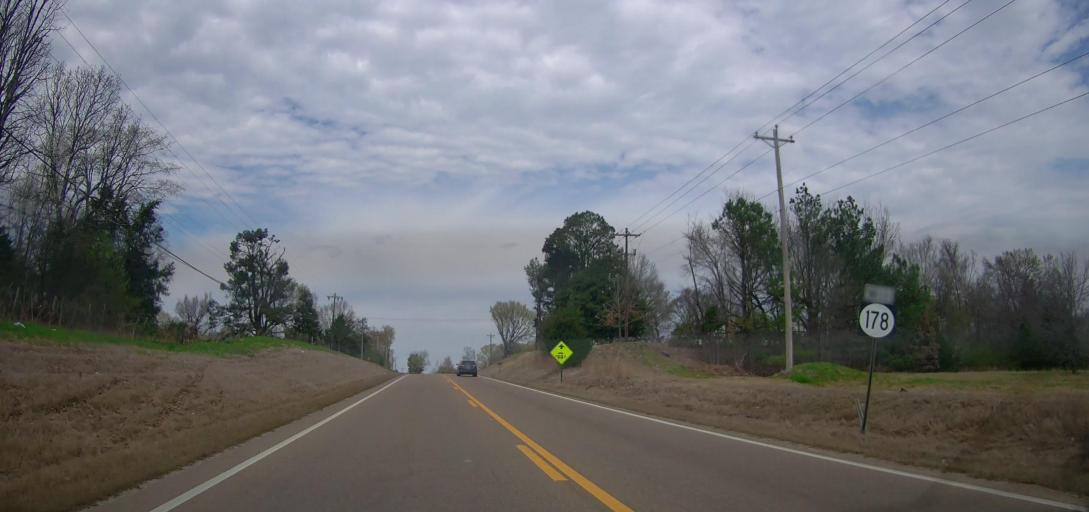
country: US
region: Mississippi
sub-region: De Soto County
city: Olive Branch
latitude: 34.9842
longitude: -89.8594
